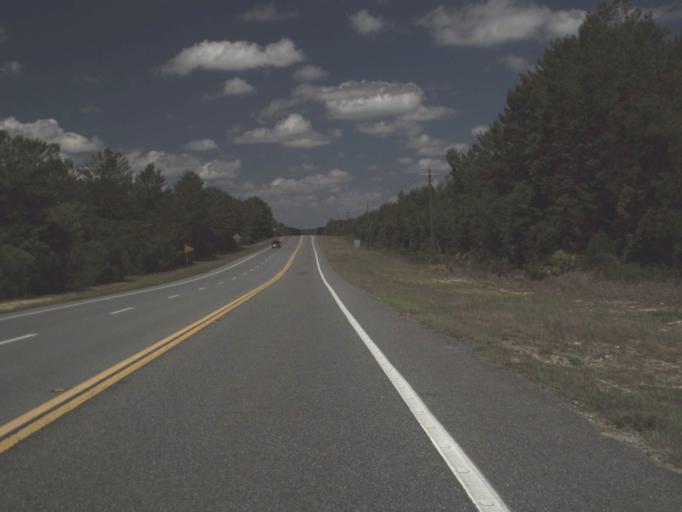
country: US
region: Florida
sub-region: Marion County
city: Silver Springs Shores
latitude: 29.1767
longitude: -81.8062
